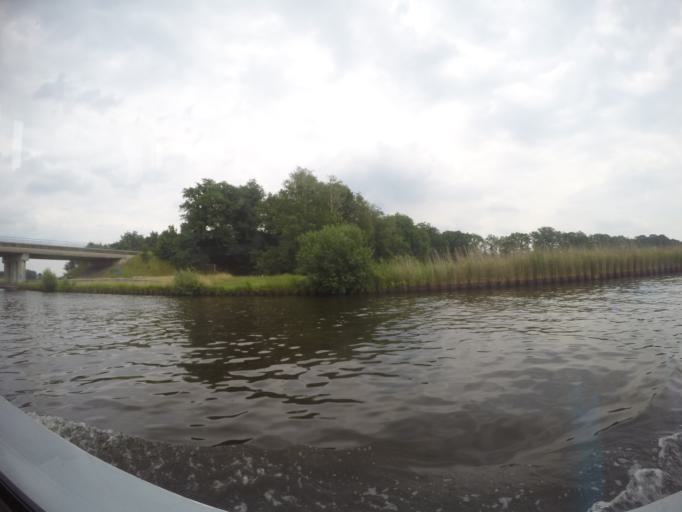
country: NL
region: Overijssel
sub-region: Gemeente Almelo
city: Almelo
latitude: 52.3086
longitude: 6.6343
